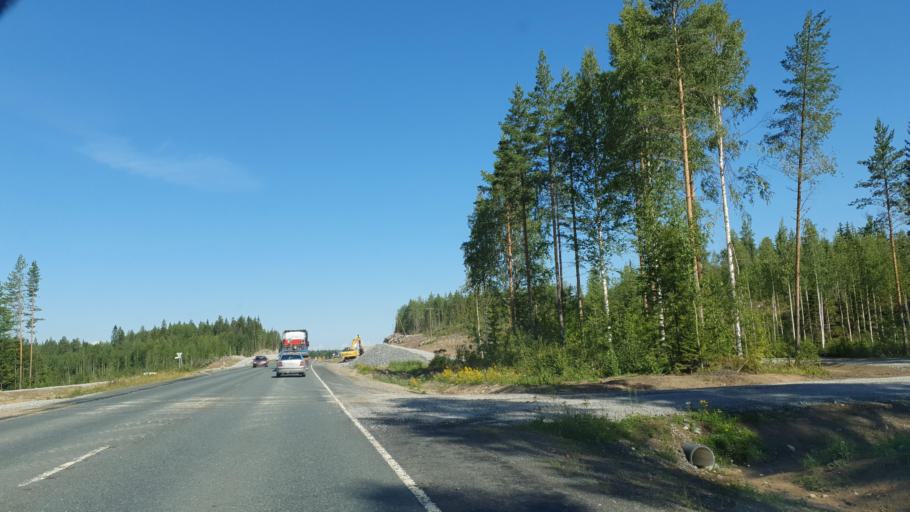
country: FI
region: Northern Savo
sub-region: Ylae-Savo
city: Lapinlahti
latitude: 63.2784
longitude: 27.4574
